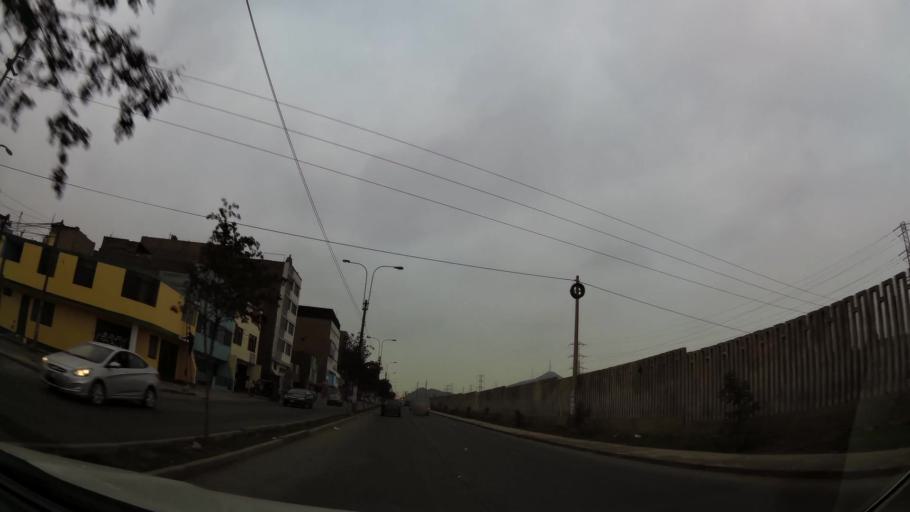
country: PE
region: Lima
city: Lima
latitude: -12.0266
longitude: -76.9955
